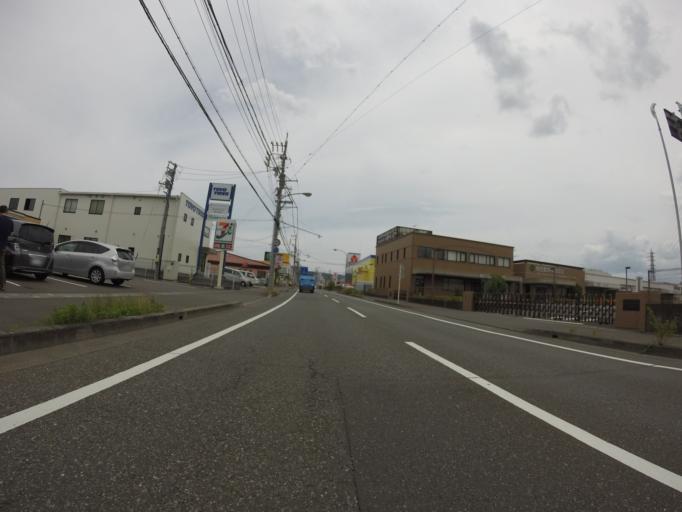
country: JP
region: Shizuoka
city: Shizuoka-shi
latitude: 34.9978
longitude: 138.4252
